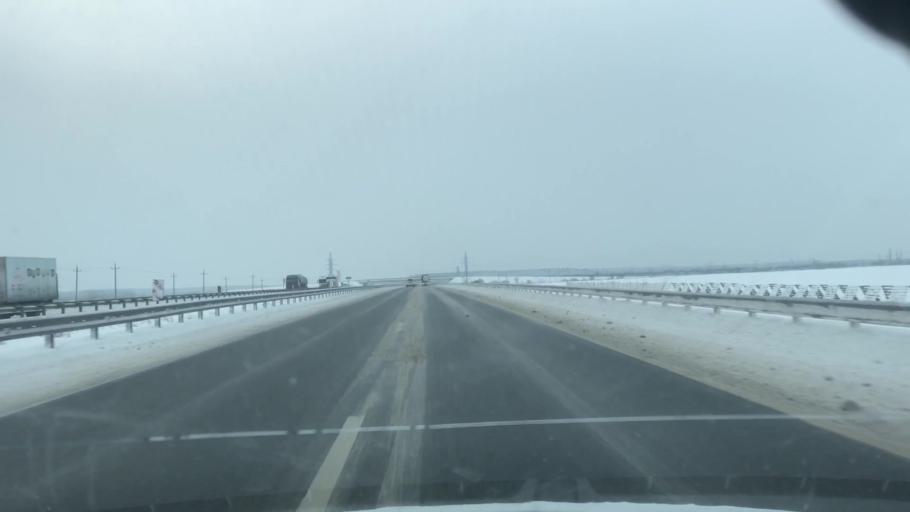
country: RU
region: Moskovskaya
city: Mikhnevo
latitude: 55.1046
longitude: 37.9266
